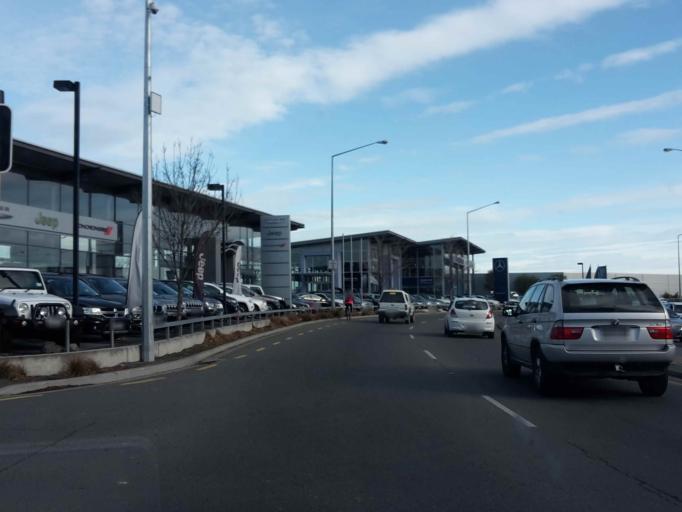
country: NZ
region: Canterbury
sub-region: Christchurch City
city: Christchurch
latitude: -43.5403
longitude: 172.6125
